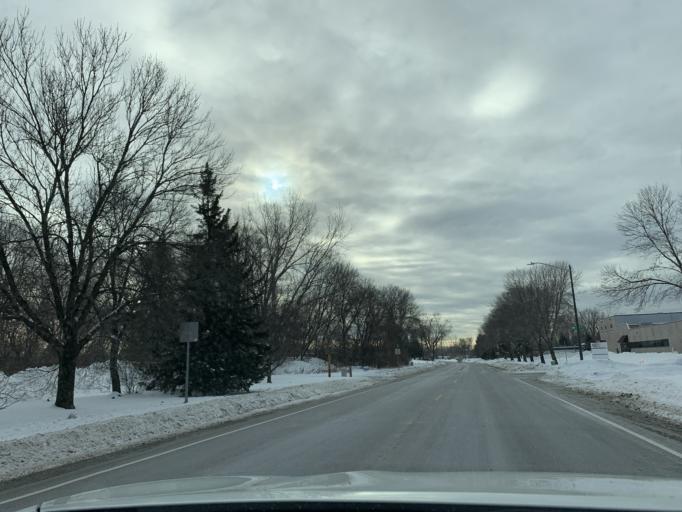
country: US
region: Minnesota
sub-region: Anoka County
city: Andover
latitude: 45.1803
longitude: -93.2981
